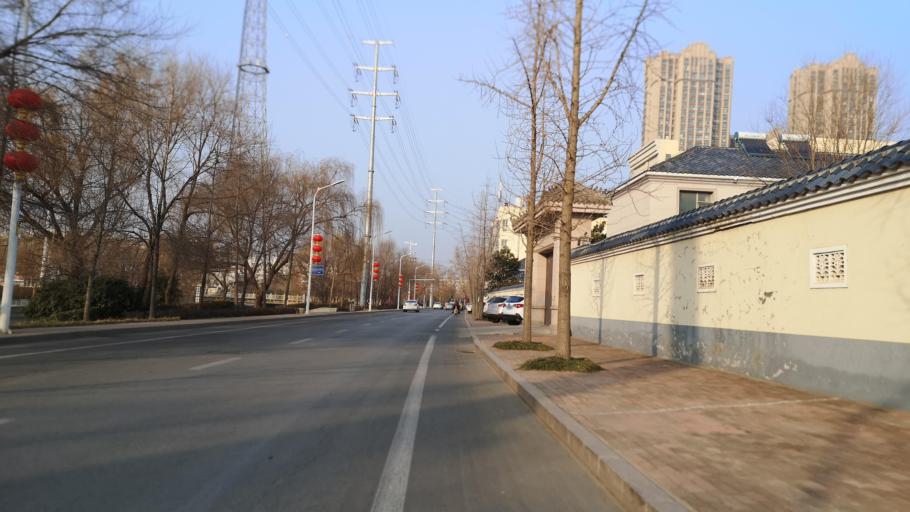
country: CN
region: Henan Sheng
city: Zhongyuanlu
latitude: 35.7782
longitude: 115.0489
